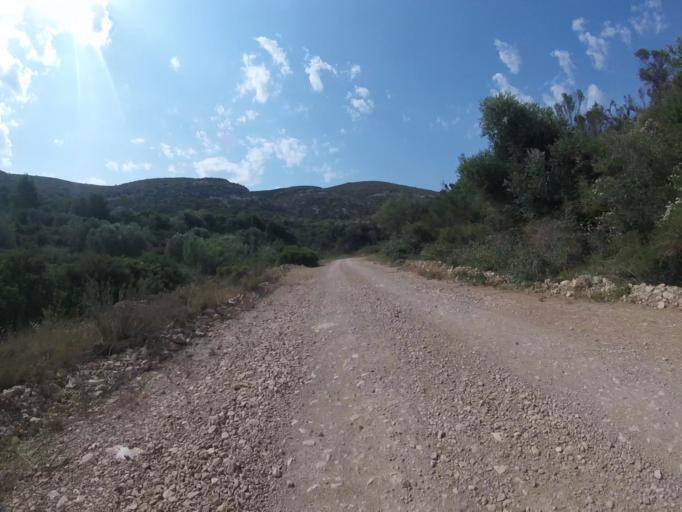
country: ES
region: Valencia
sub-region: Provincia de Castello
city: Alcala de Xivert
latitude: 40.3177
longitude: 0.1862
